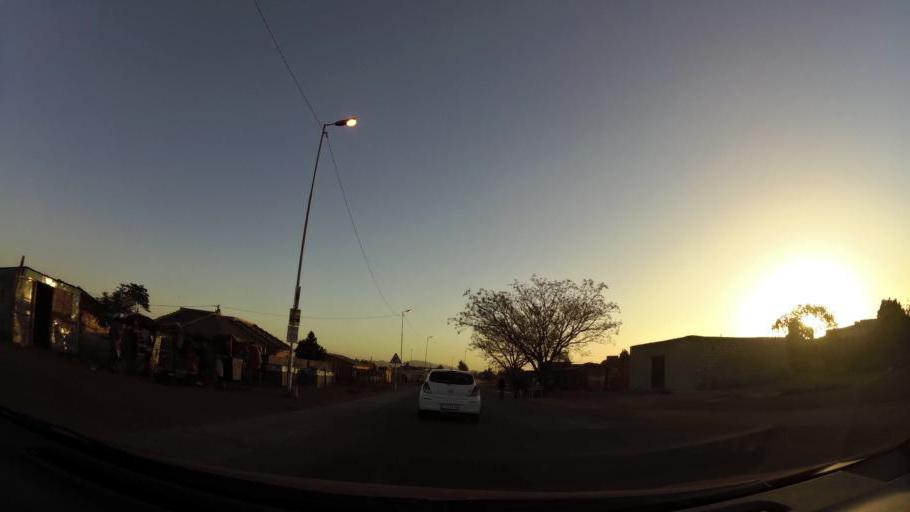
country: ZA
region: Gauteng
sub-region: City of Tshwane Metropolitan Municipality
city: Mabopane
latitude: -25.5814
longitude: 28.0871
